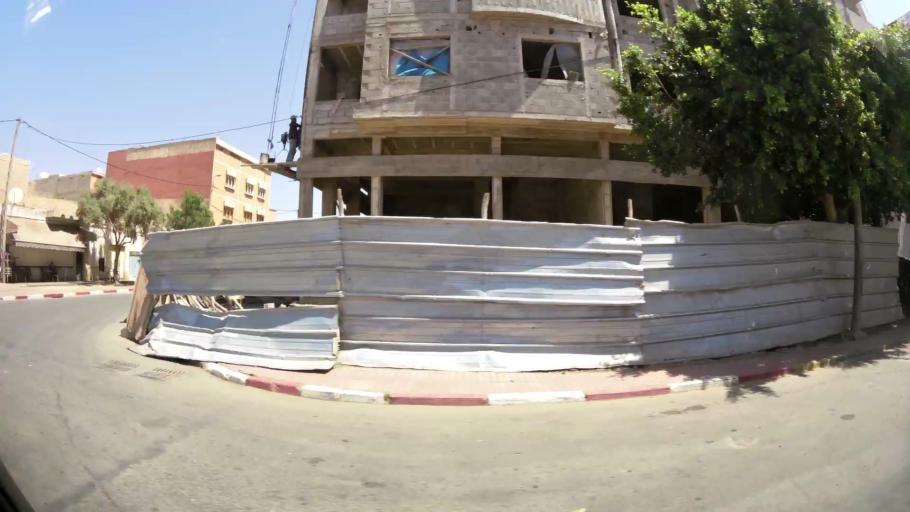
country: MA
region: Souss-Massa-Draa
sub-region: Inezgane-Ait Mellou
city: Inezgane
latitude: 30.3412
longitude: -9.4969
